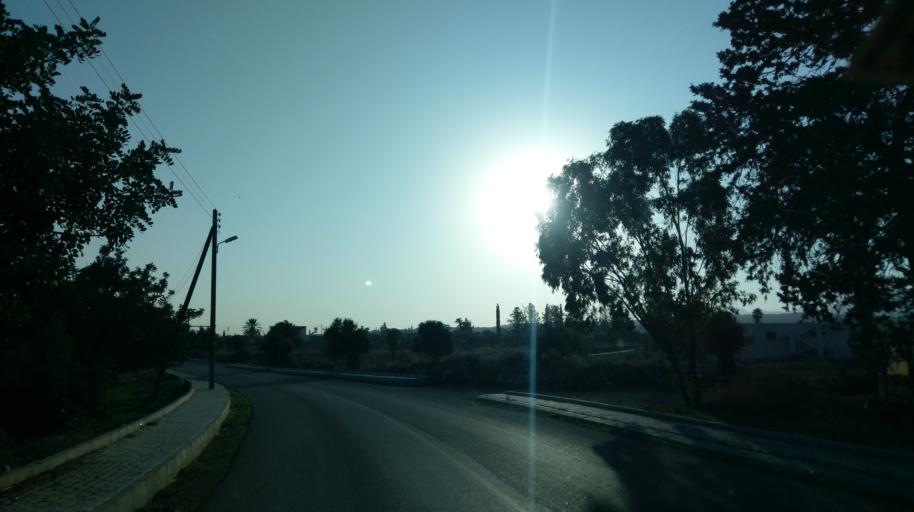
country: CY
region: Ammochostos
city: Leonarisso
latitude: 35.4163
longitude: 34.0010
